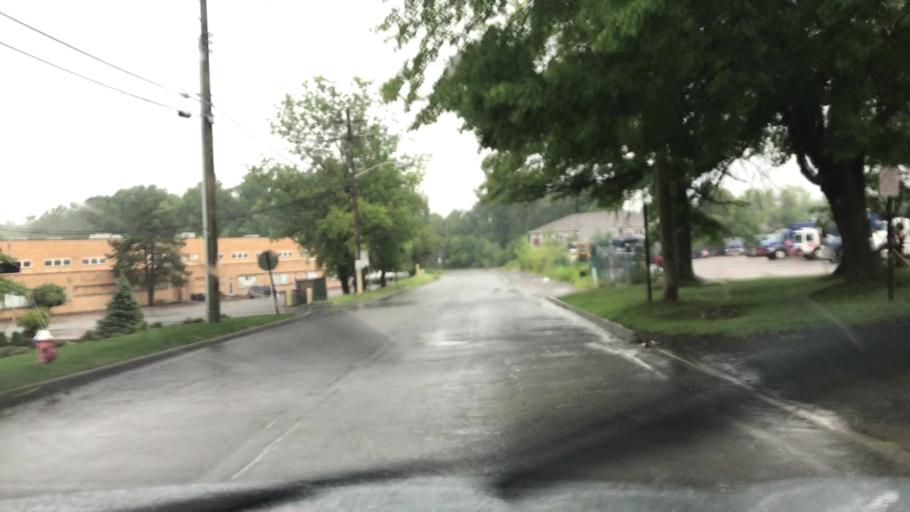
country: US
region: New Jersey
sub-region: Bergen County
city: Closter
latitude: 40.9788
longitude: -73.9603
